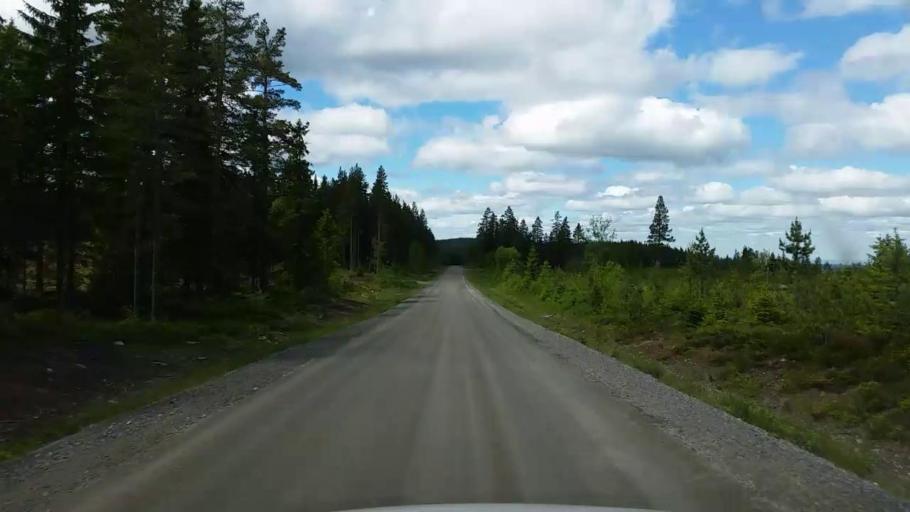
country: SE
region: Gaevleborg
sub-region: Bollnas Kommun
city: Vittsjo
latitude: 61.1790
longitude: 16.1461
